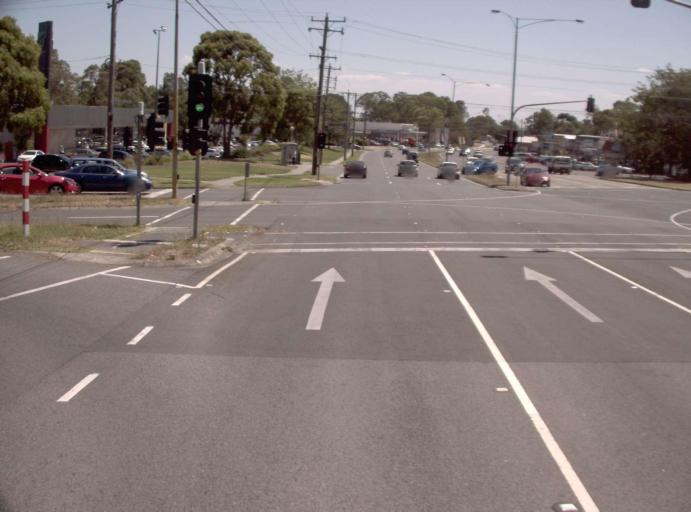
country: AU
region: Victoria
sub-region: Knox
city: Ferntree Gully
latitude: -37.8887
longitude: 145.2952
